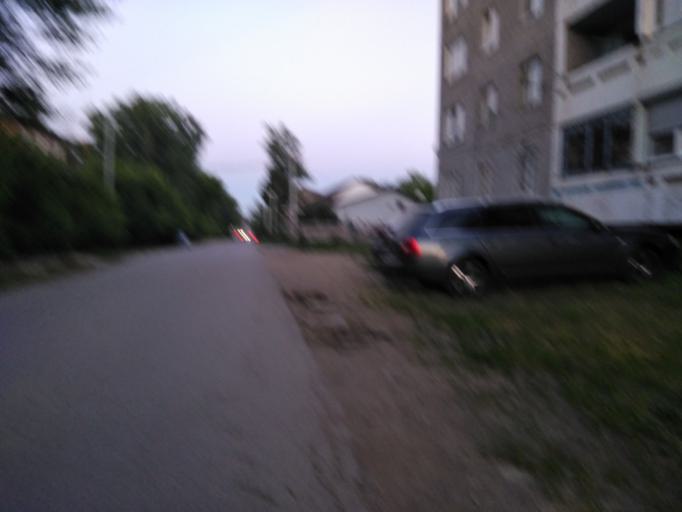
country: RU
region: Tula
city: Lomintsevskiy
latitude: 53.9379
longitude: 37.6281
